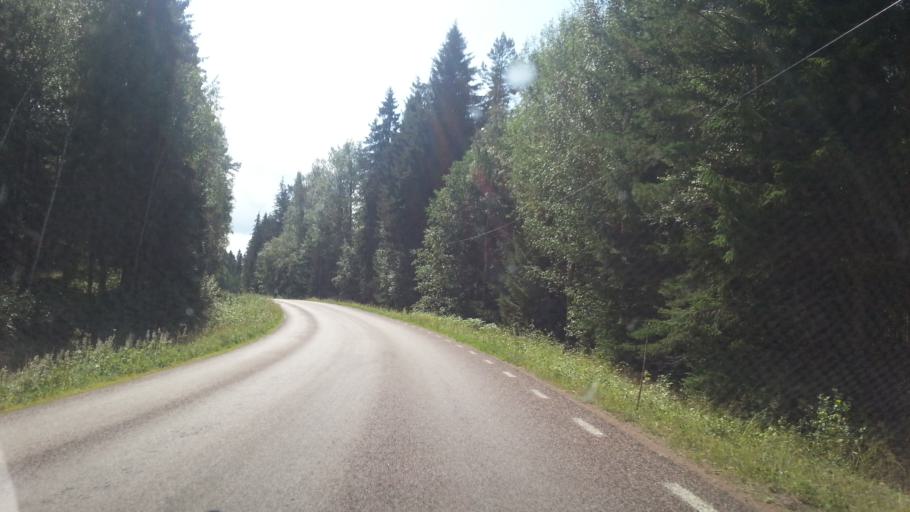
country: SE
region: Dalarna
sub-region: Faluns Kommun
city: Falun
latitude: 60.6469
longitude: 15.7851
